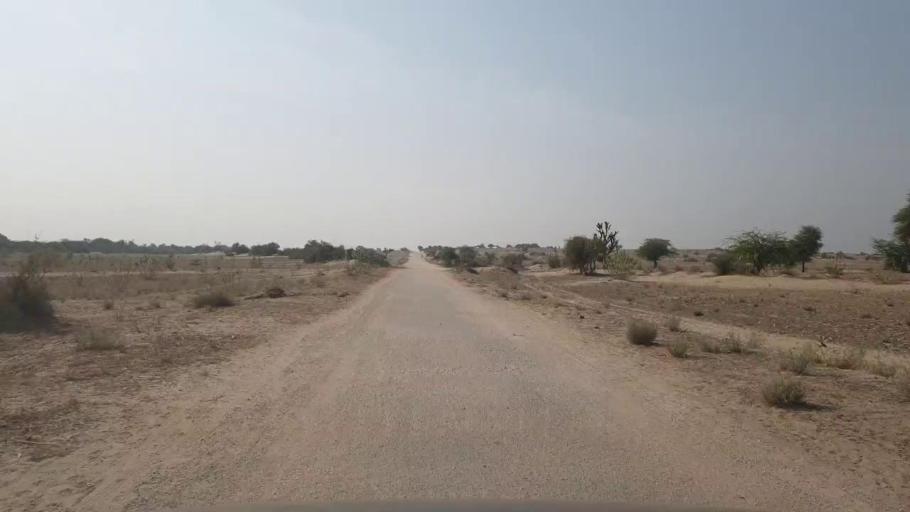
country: PK
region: Sindh
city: Umarkot
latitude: 25.3054
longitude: 69.7284
